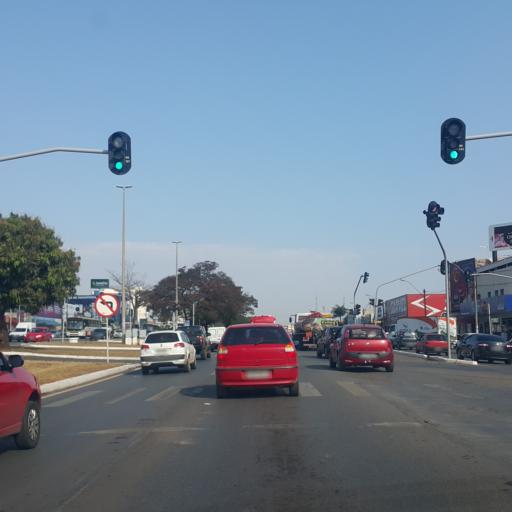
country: BR
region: Federal District
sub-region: Brasilia
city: Brasilia
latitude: -15.8469
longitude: -48.0434
